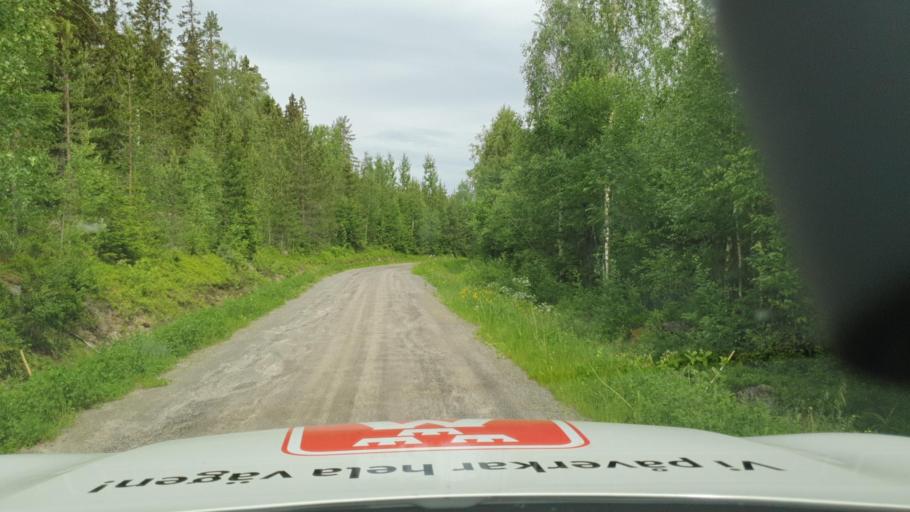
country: SE
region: Vaesterbotten
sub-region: Robertsfors Kommun
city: Robertsfors
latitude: 64.2657
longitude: 20.6901
